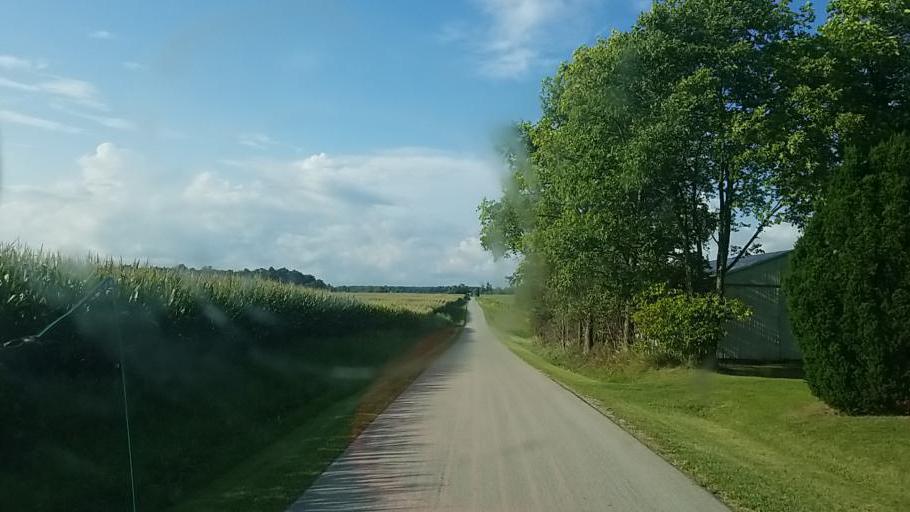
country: US
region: Ohio
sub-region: Wyandot County
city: Upper Sandusky
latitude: 40.8270
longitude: -83.1602
